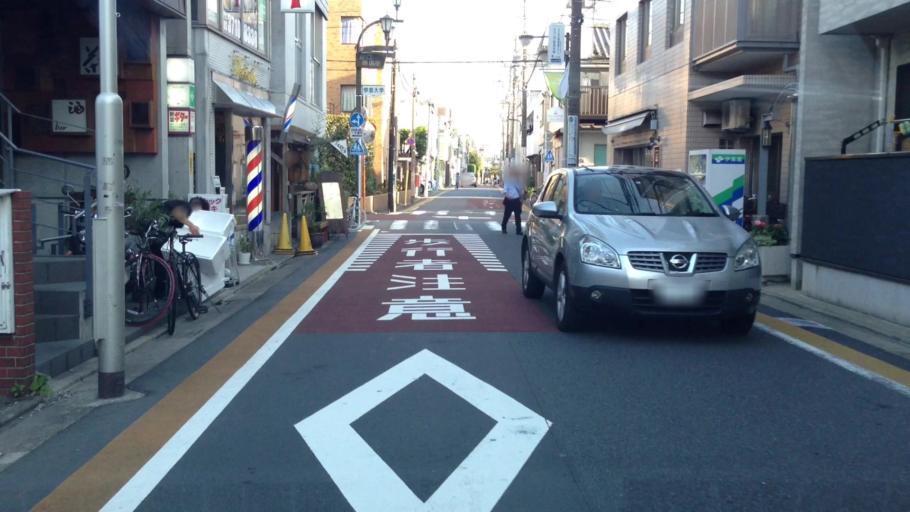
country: JP
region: Tokyo
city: Tokyo
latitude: 35.6283
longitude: 139.6868
